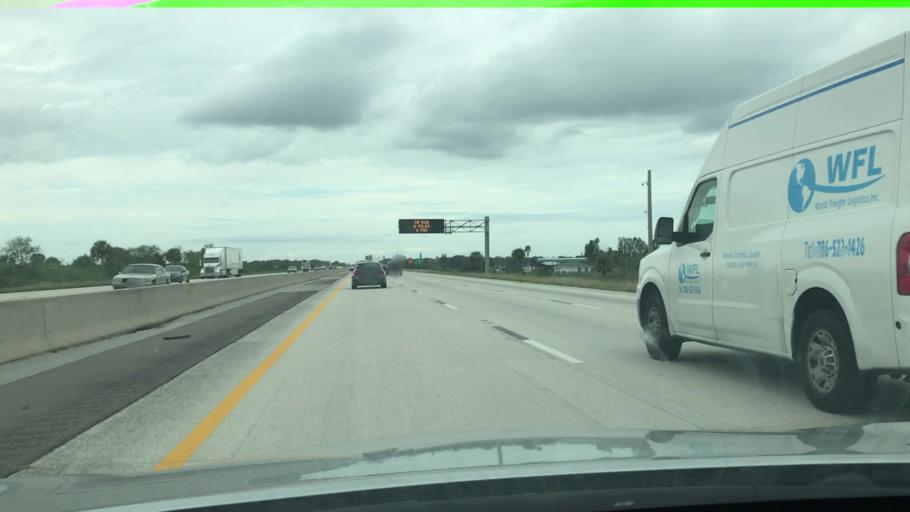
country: US
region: Florida
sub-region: Brevard County
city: Cocoa West
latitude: 28.3380
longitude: -80.7803
